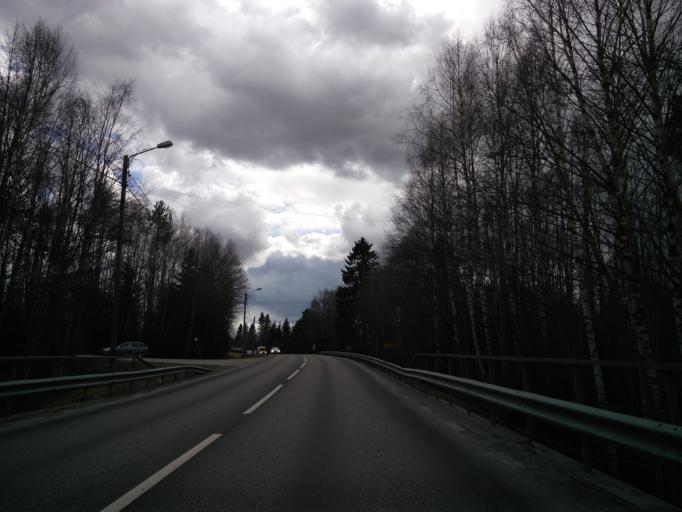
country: SE
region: Vaesternorrland
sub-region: Sundsvalls Kommun
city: Vi
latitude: 62.4582
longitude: 17.1621
